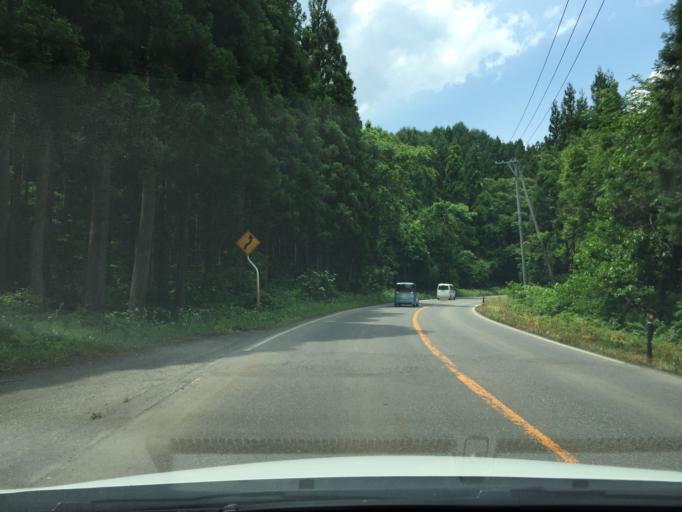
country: JP
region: Fukushima
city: Inawashiro
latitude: 37.6113
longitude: 140.1181
